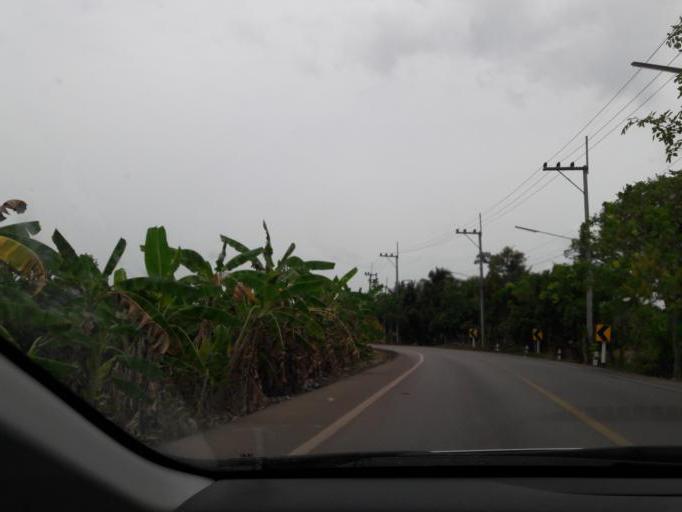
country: TH
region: Samut Sakhon
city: Ban Phaeo
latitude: 13.5807
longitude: 100.0384
